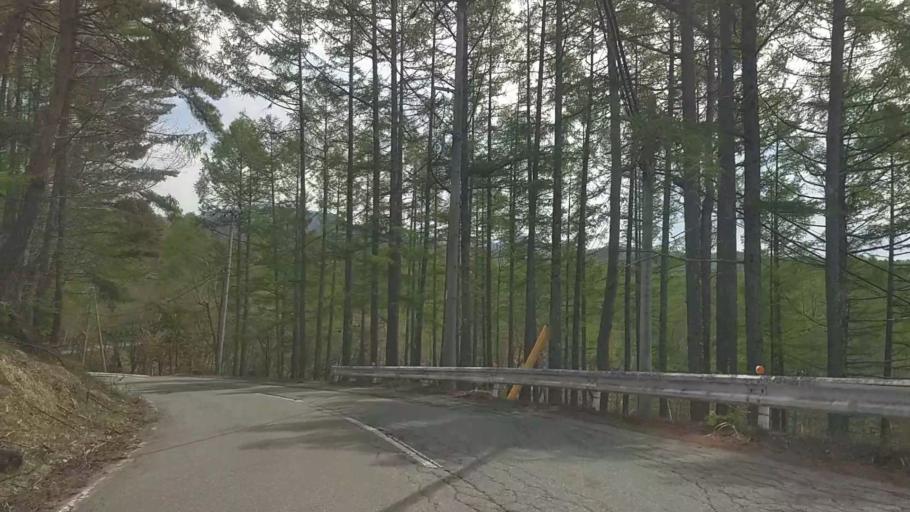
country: JP
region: Nagano
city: Chino
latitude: 36.0426
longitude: 138.2927
